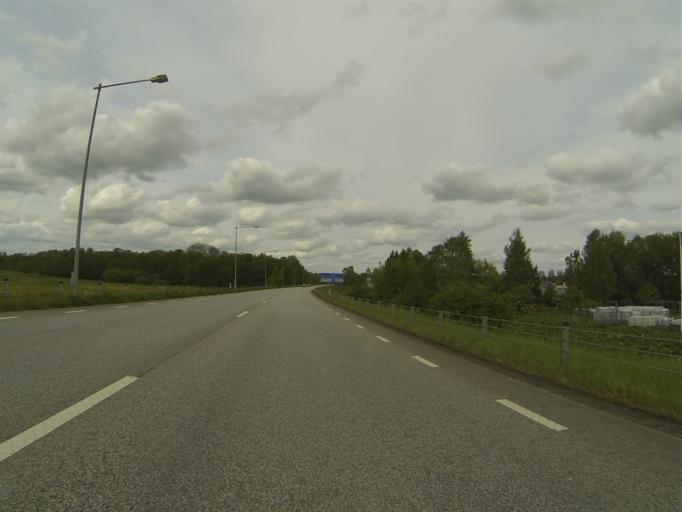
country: SE
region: Skane
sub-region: Sjobo Kommun
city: Sjoebo
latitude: 55.6392
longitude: 13.6834
